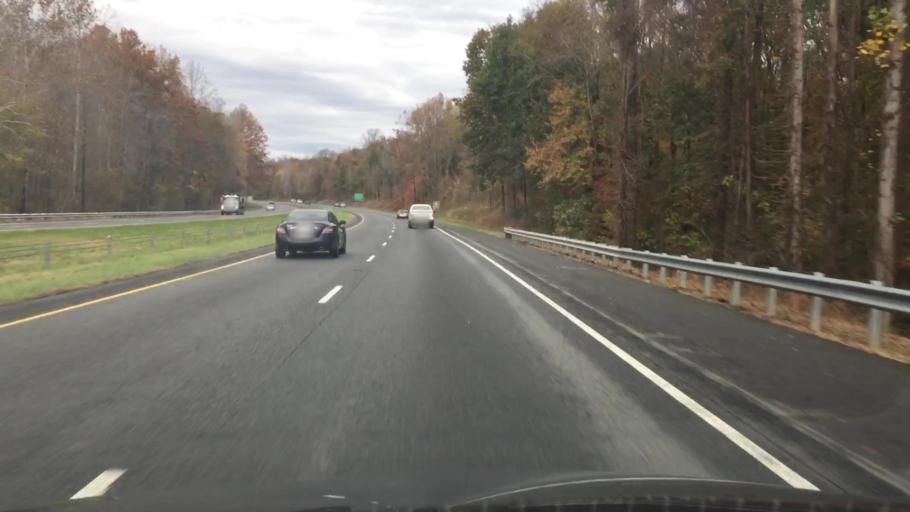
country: US
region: North Carolina
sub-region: Rockingham County
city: Reidsville
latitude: 36.2986
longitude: -79.6410
